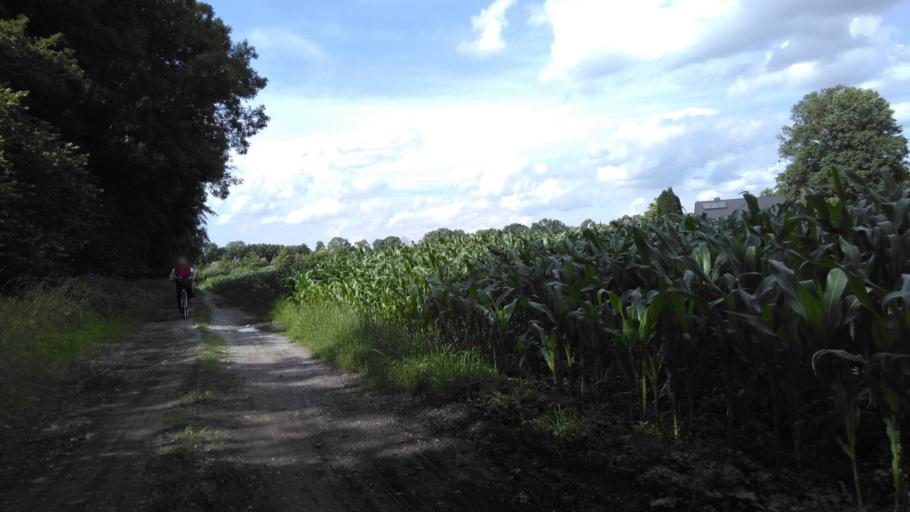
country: DE
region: North Rhine-Westphalia
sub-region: Regierungsbezirk Detmold
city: Verl
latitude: 51.8830
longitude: 8.4741
